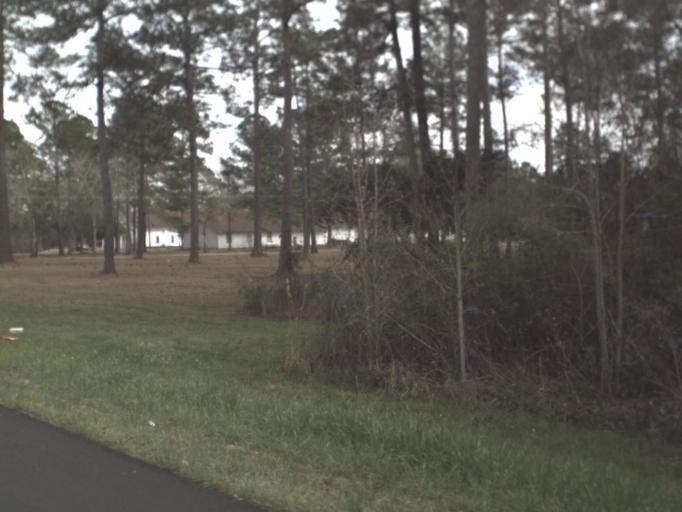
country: US
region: Florida
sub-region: Gadsden County
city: Midway
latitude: 30.3964
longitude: -84.6072
